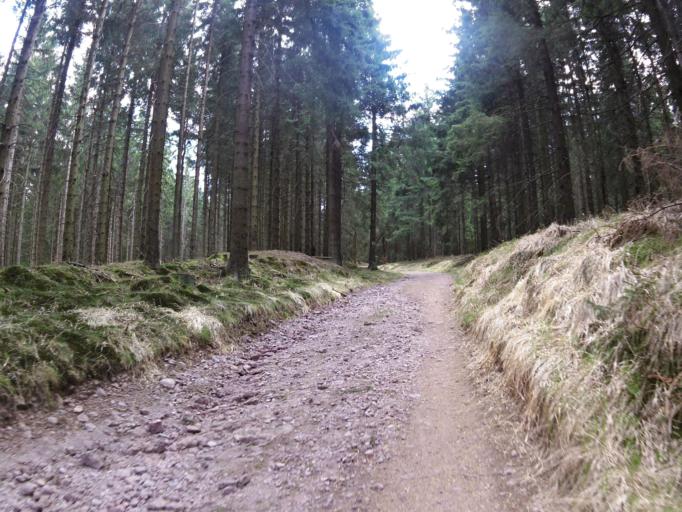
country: DE
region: Thuringia
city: Unterschonau
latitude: 50.7536
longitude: 10.5677
